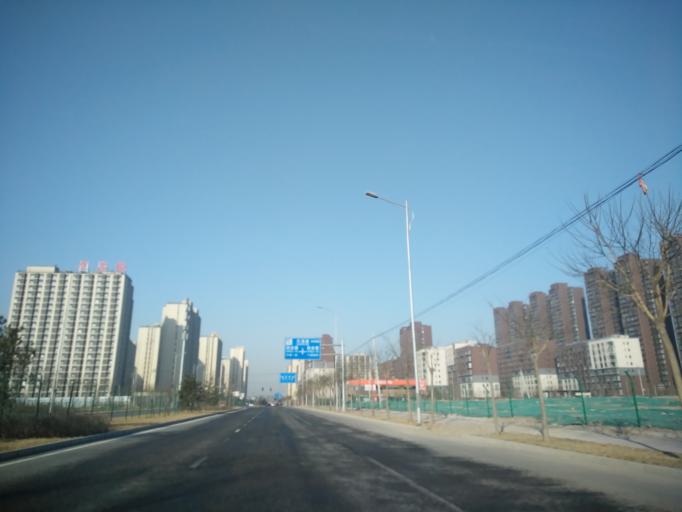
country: CN
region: Beijing
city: Yinghai
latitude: 39.7513
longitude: 116.4856
